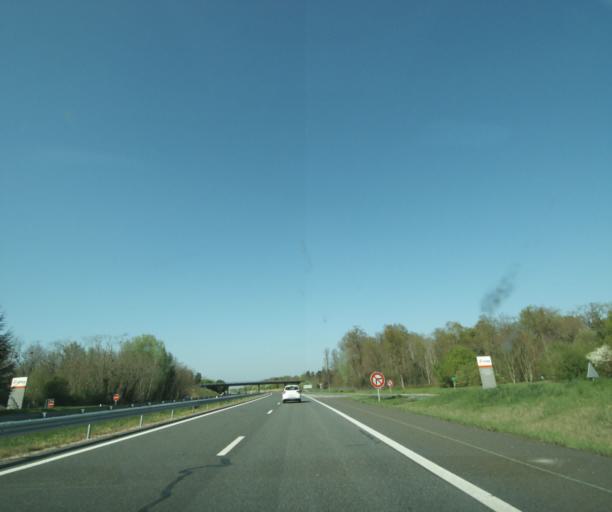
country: FR
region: Centre
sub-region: Departement du Loiret
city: Vimory
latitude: 47.9778
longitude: 2.6742
